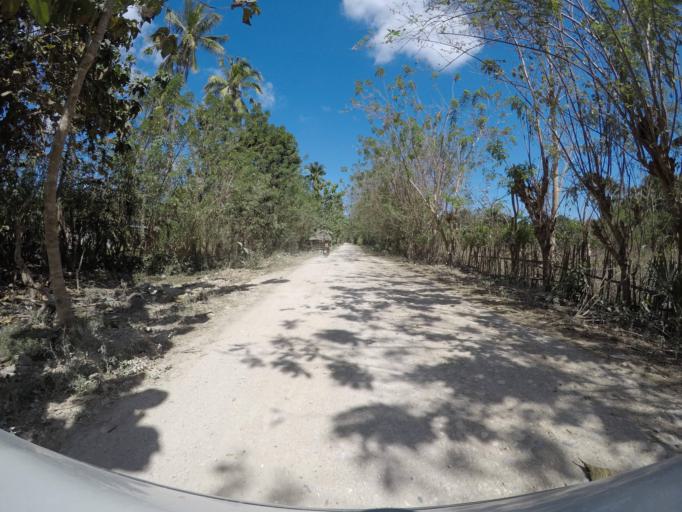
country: TL
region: Viqueque
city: Viqueque
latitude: -8.9294
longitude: 126.4092
